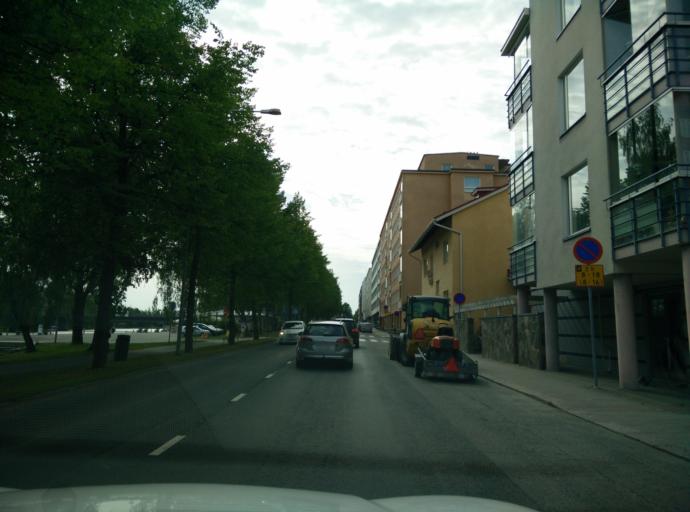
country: FI
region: Haeme
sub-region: Haemeenlinna
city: Haemeenlinna
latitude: 60.9995
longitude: 24.4693
